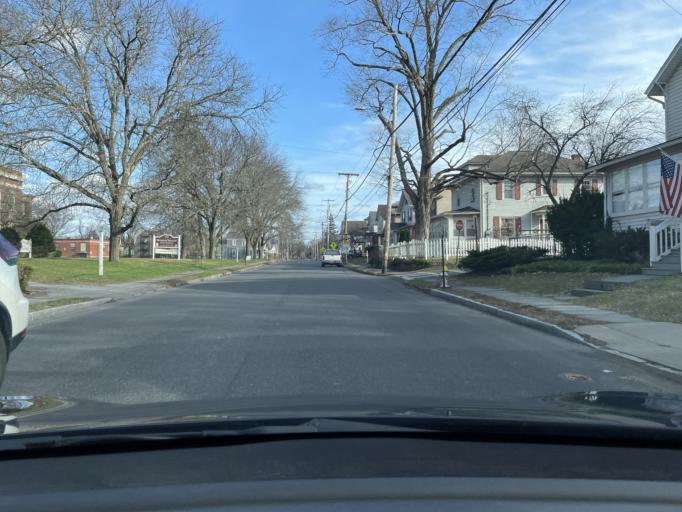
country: US
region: New York
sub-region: Ulster County
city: Kingston
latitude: 41.9263
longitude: -74.0170
